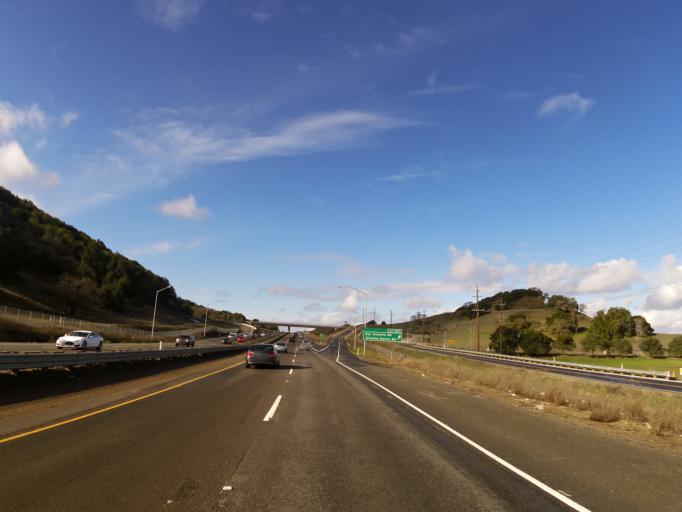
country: US
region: California
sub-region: Marin County
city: Novato
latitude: 38.1603
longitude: -122.5713
